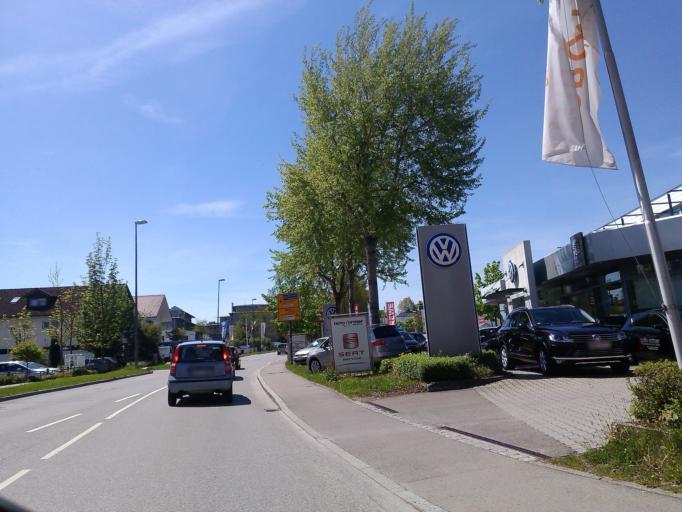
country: DE
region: Bavaria
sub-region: Upper Bavaria
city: Starnberg
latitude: 48.0043
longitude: 11.3500
